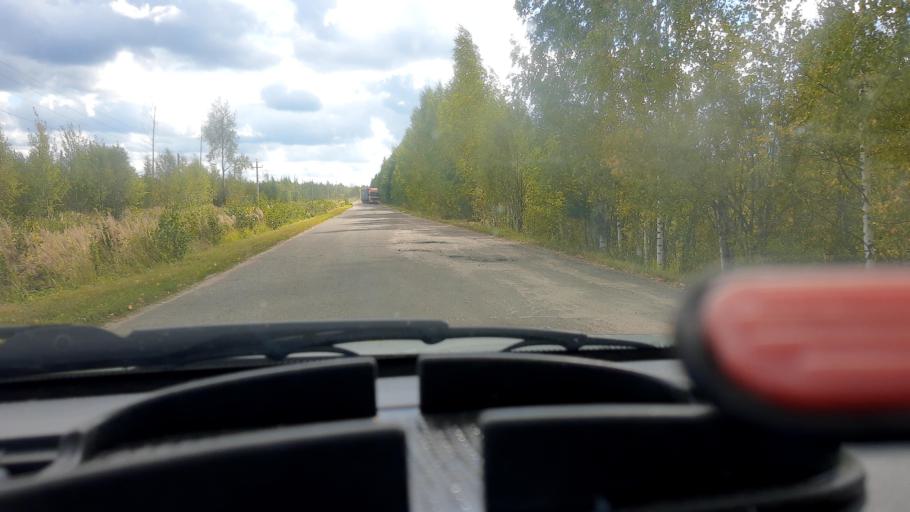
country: RU
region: Mariy-El
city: Kilemary
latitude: 56.8891
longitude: 46.7583
